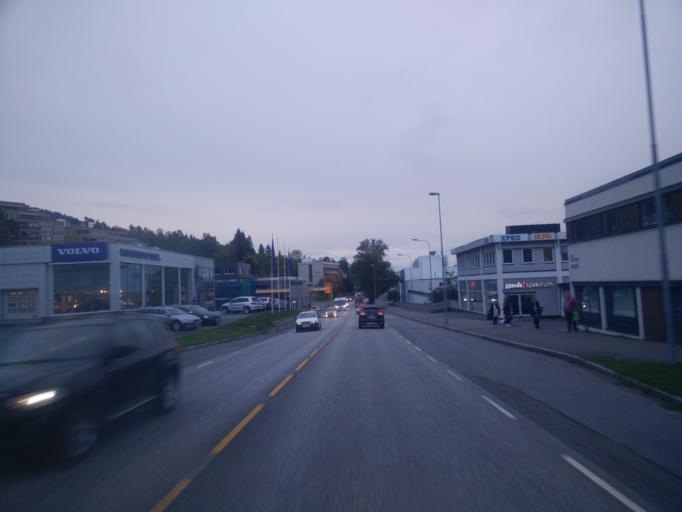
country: NO
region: More og Romsdal
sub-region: Molde
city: Molde
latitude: 62.7390
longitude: 7.1831
